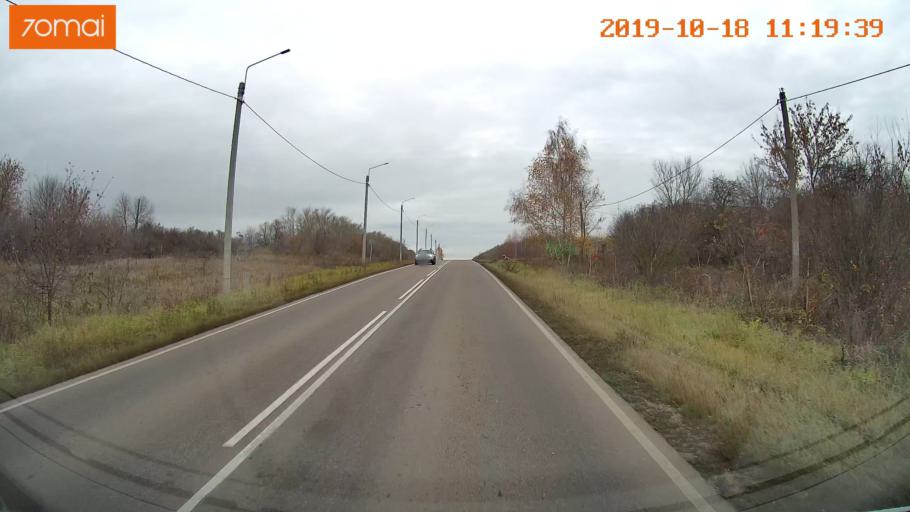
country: RU
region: Tula
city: Kimovsk
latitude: 54.0488
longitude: 38.5549
